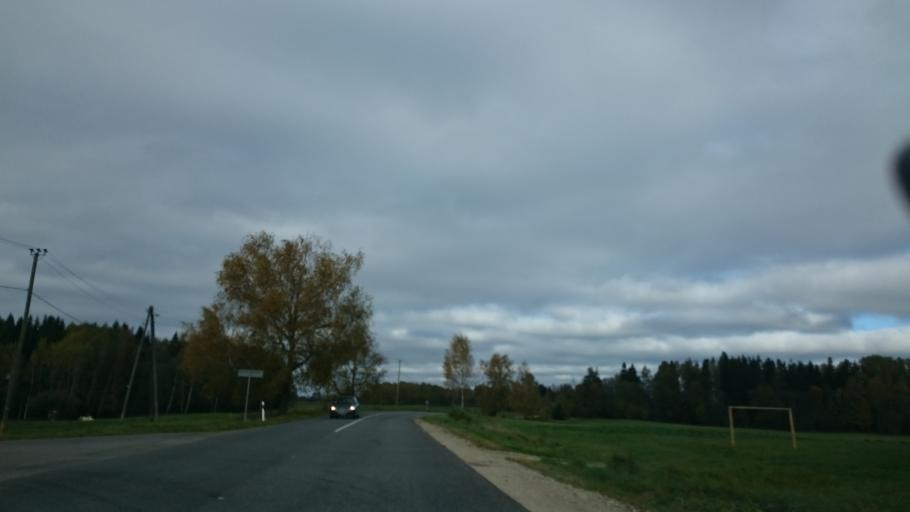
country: LV
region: Cesu Rajons
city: Cesis
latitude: 57.2828
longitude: 25.2651
